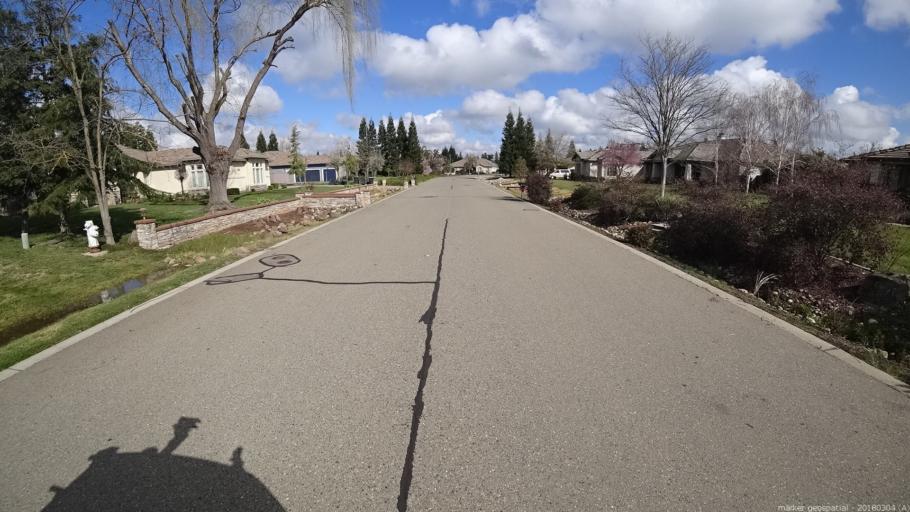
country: US
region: California
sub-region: Sacramento County
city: Vineyard
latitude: 38.4672
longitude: -121.3148
